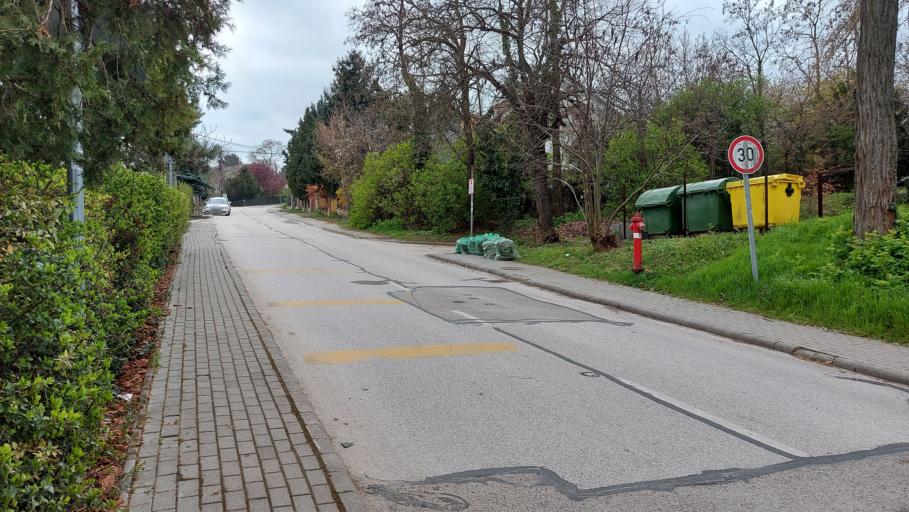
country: HU
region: Pest
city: Budaors
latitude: 47.4378
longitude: 18.9681
